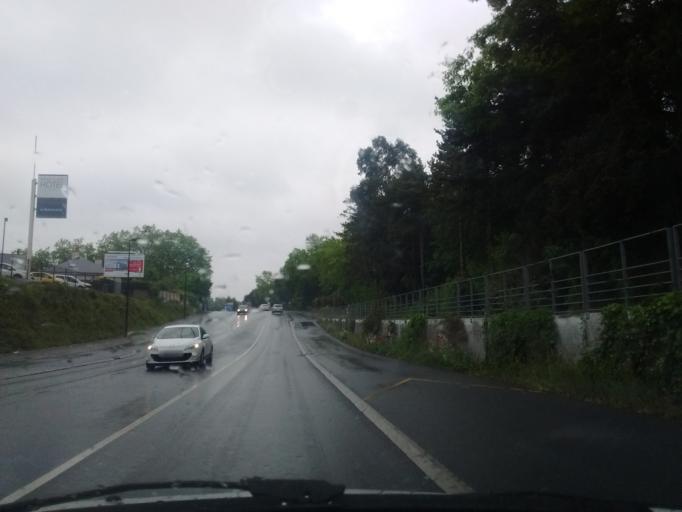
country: FR
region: Pays de la Loire
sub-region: Departement de la Loire-Atlantique
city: Sainte-Luce-sur-Loire
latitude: 47.2573
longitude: -1.5289
